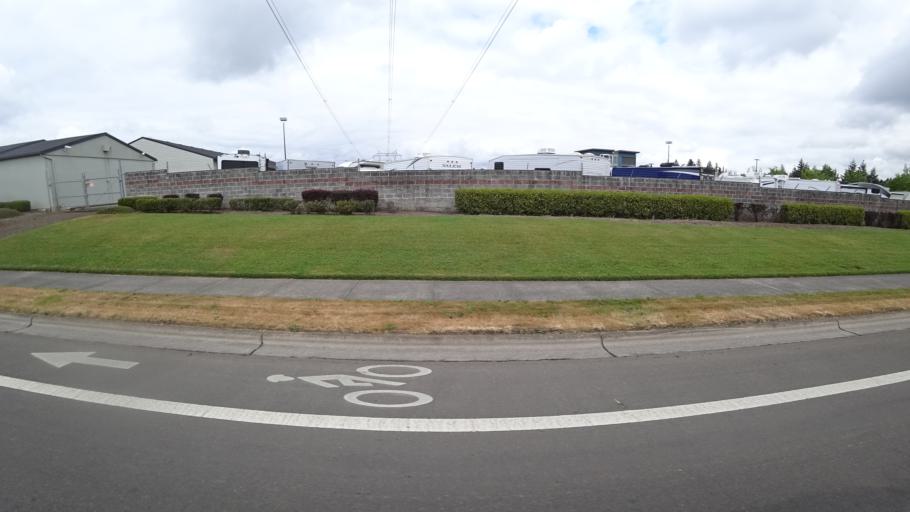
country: US
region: Oregon
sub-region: Washington County
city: Rockcreek
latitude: 45.5374
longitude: -122.8959
